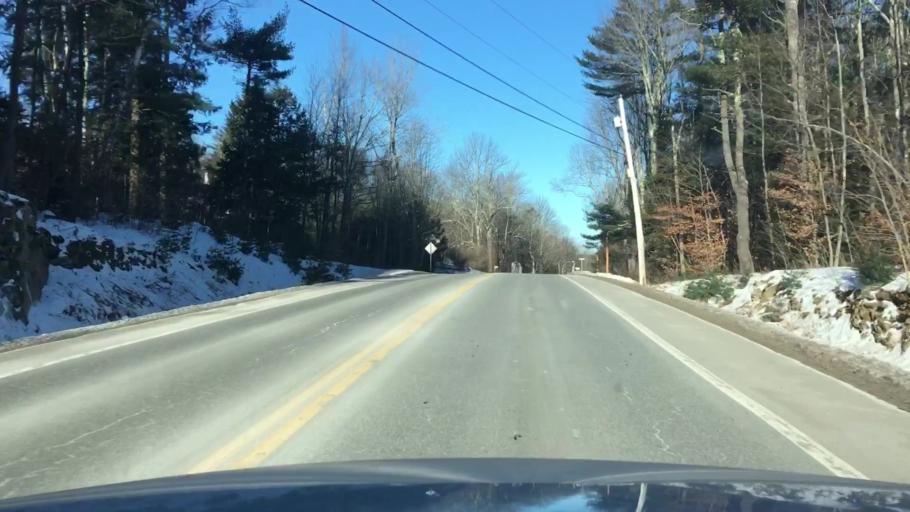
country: US
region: Maine
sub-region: Cumberland County
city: Freeport
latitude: 43.8785
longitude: -70.1089
